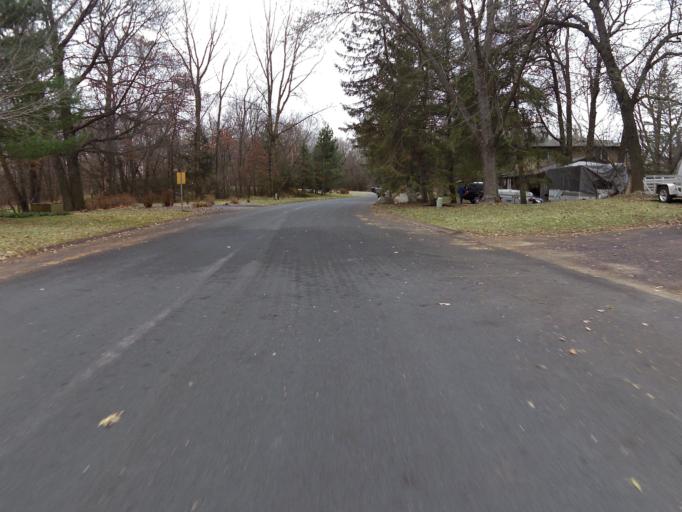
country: US
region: Minnesota
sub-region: Washington County
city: Lake Elmo
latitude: 44.9799
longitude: -92.8717
